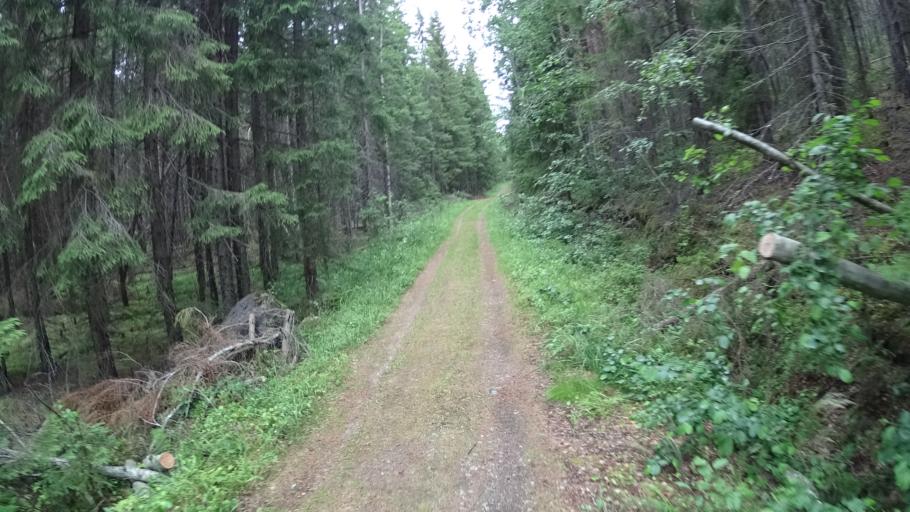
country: FI
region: Southern Savonia
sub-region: Mikkeli
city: Maentyharju
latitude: 61.1861
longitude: 26.8284
